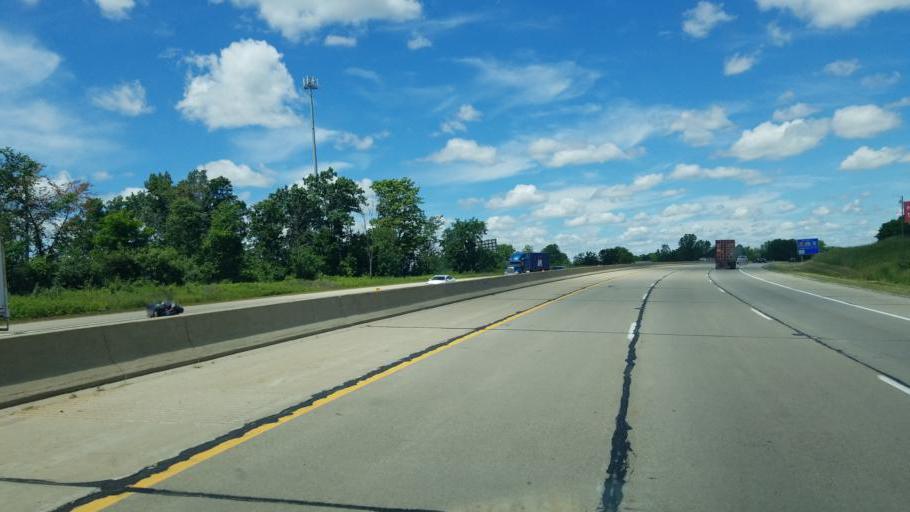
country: US
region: Michigan
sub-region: Livingston County
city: Howell
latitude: 42.5856
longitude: -83.9269
